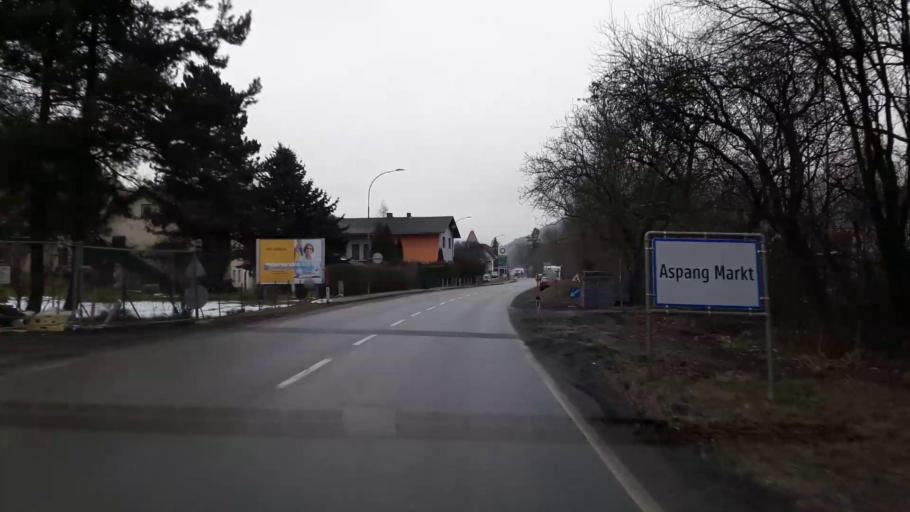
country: AT
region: Lower Austria
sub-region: Politischer Bezirk Neunkirchen
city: Thomasberg
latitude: 47.5659
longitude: 16.0975
